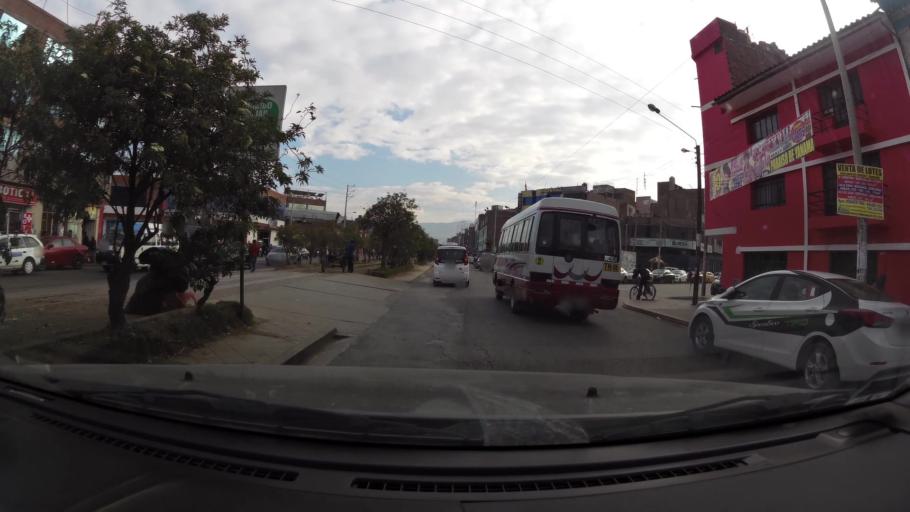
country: PE
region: Junin
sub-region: Provincia de Huancayo
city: Huancayo
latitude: -12.0743
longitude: -75.2050
